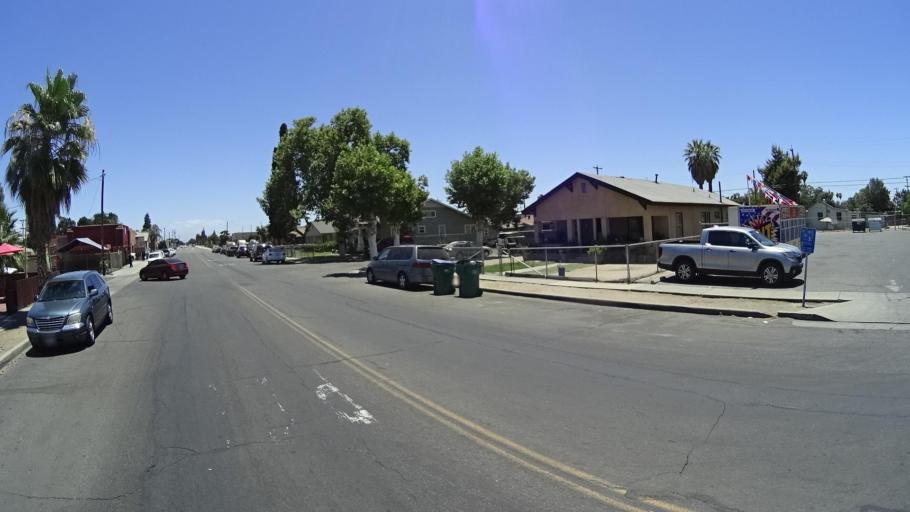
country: US
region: California
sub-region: Fresno County
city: Fresno
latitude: 36.7070
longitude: -119.7564
